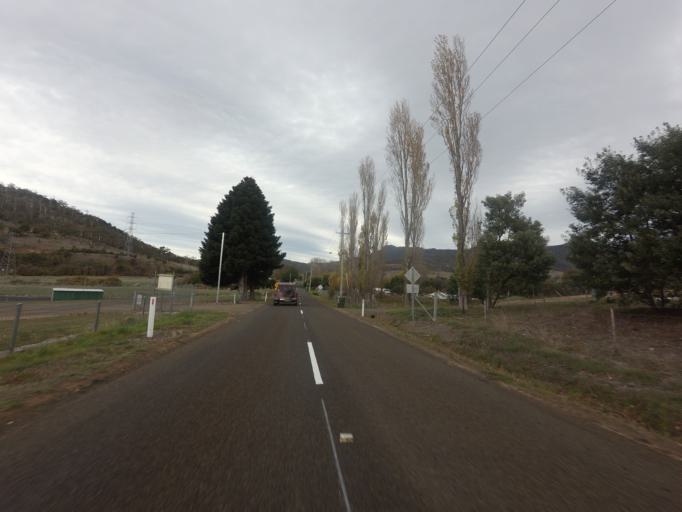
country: AU
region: Tasmania
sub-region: Brighton
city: Bridgewater
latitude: -42.6563
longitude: 147.1260
